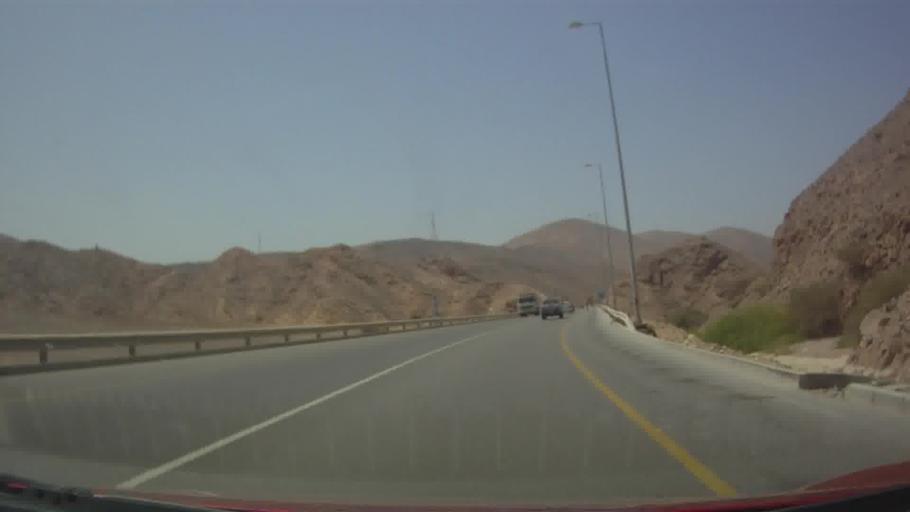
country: OM
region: Muhafazat Masqat
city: Muscat
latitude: 23.5239
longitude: 58.6390
